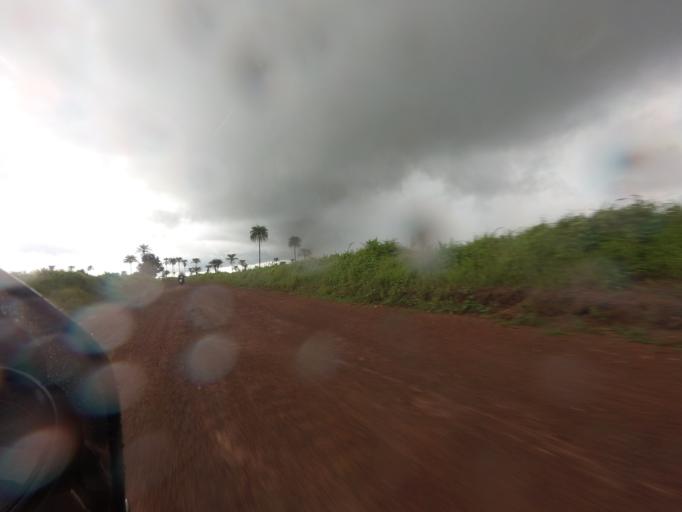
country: SL
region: Northern Province
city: Kukuna
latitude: 9.2622
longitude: -12.7476
